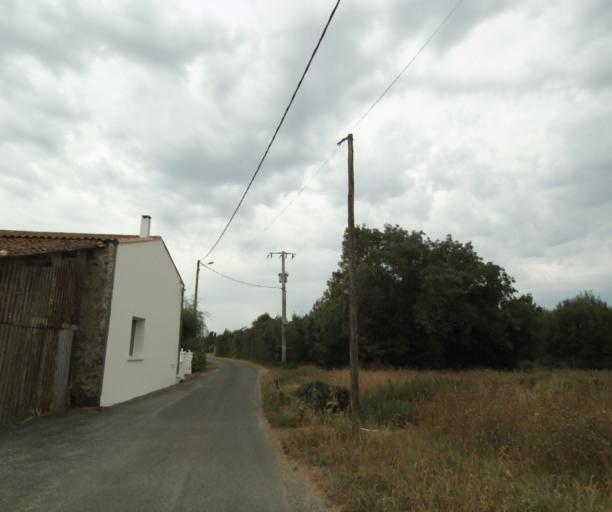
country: FR
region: Poitou-Charentes
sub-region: Departement de la Charente-Maritime
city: Tonnay-Charente
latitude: 45.9647
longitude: -0.8770
